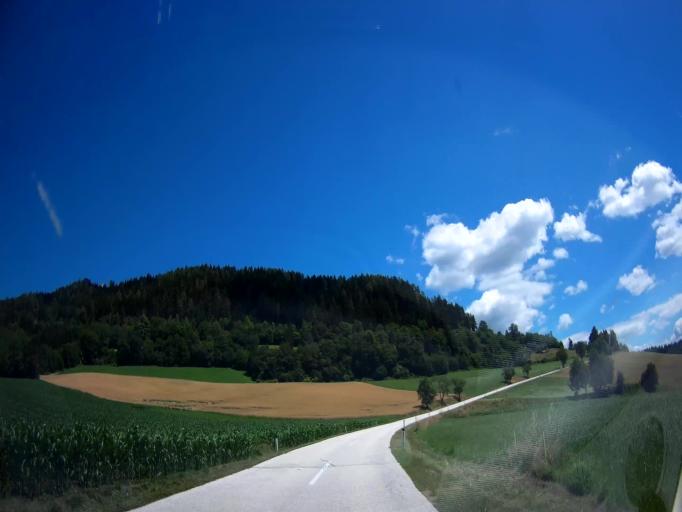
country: AT
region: Carinthia
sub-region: Politischer Bezirk Sankt Veit an der Glan
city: St. Georgen am Laengsee
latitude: 46.7225
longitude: 14.4180
